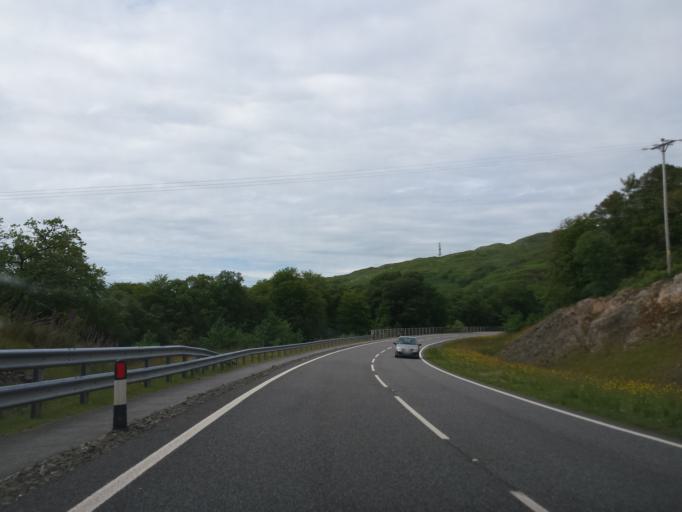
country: GB
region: Scotland
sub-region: Argyll and Bute
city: Isle Of Mull
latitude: 56.9075
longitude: -5.8218
